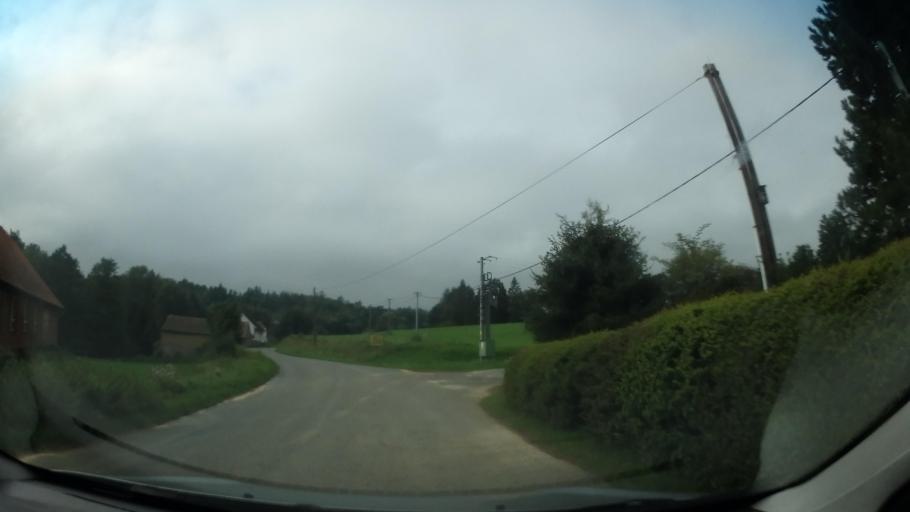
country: CZ
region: Central Bohemia
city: Sedlcany
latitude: 49.7158
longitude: 14.4130
